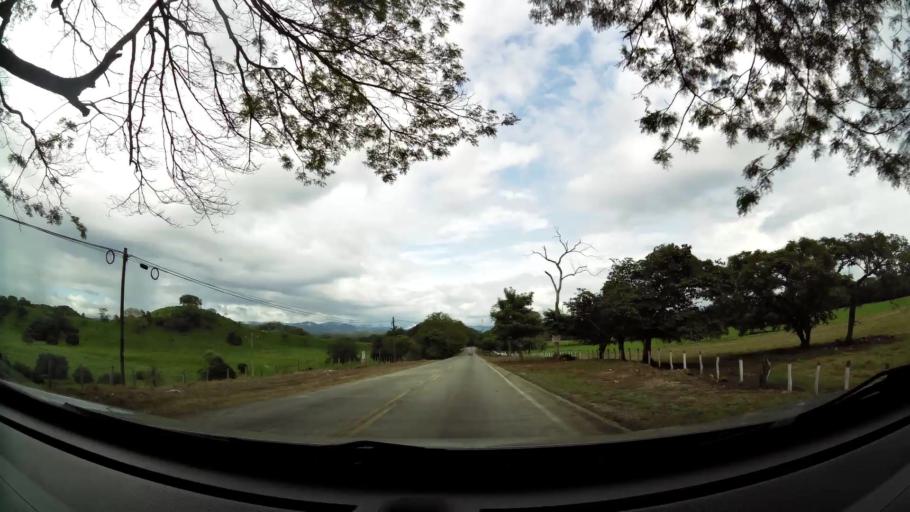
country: CR
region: Guanacaste
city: Juntas
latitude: 10.2635
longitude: -85.0327
